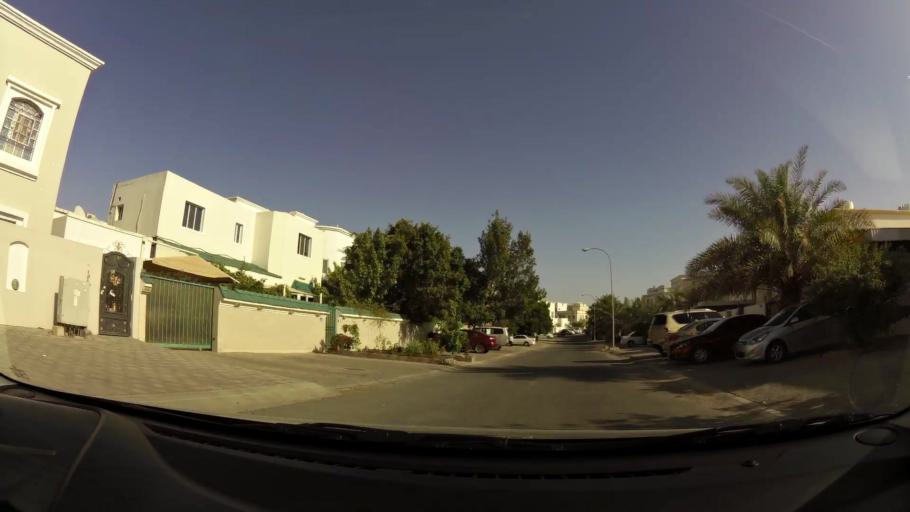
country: OM
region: Muhafazat Masqat
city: As Sib al Jadidah
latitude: 23.6005
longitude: 58.2163
